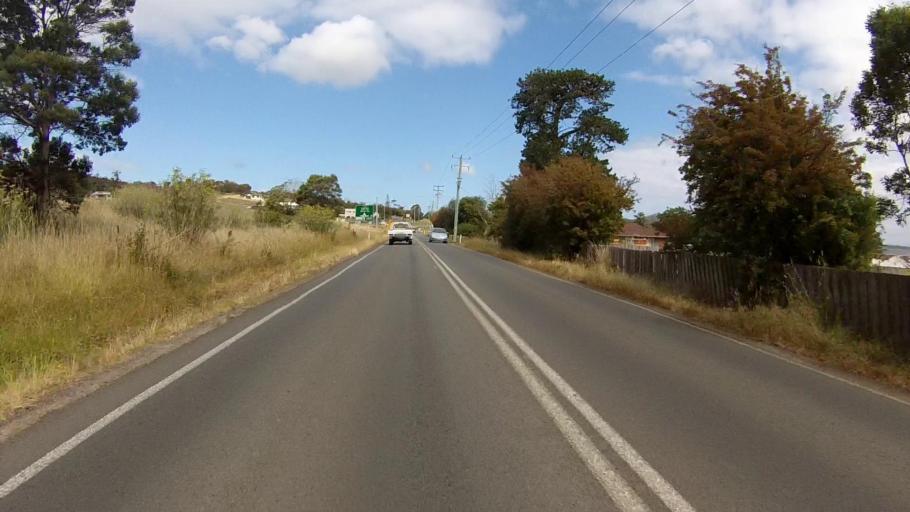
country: AU
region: Tasmania
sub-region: Clarence
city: Rokeby
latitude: -42.9044
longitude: 147.4521
